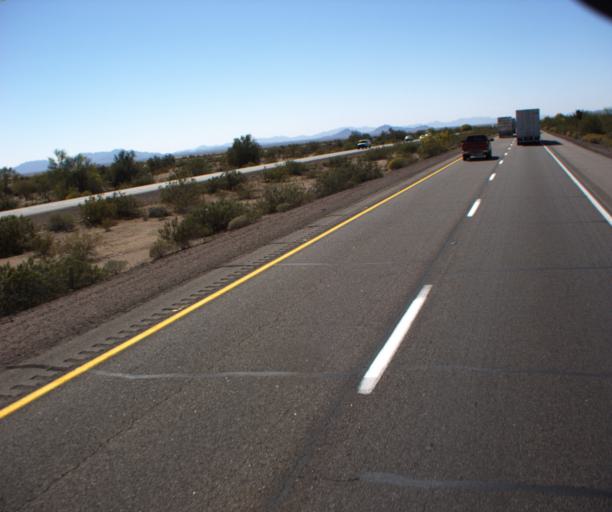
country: US
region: Arizona
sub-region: Yuma County
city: Wellton
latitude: 32.7204
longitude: -113.7773
